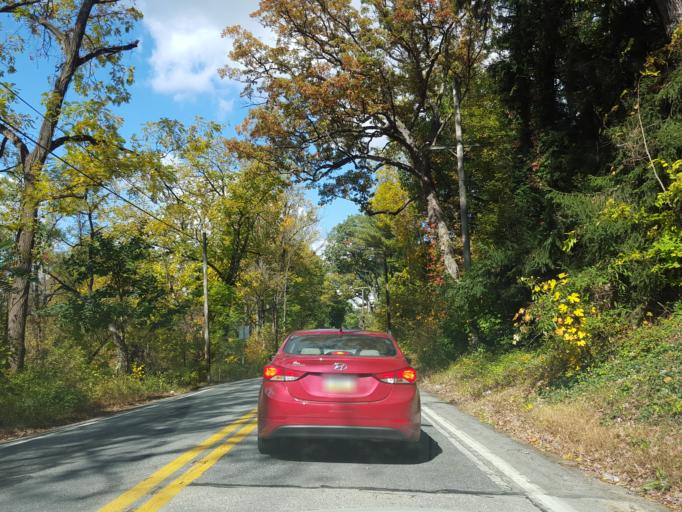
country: US
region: Pennsylvania
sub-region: York County
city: Valley View
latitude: 39.9510
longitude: -76.6813
